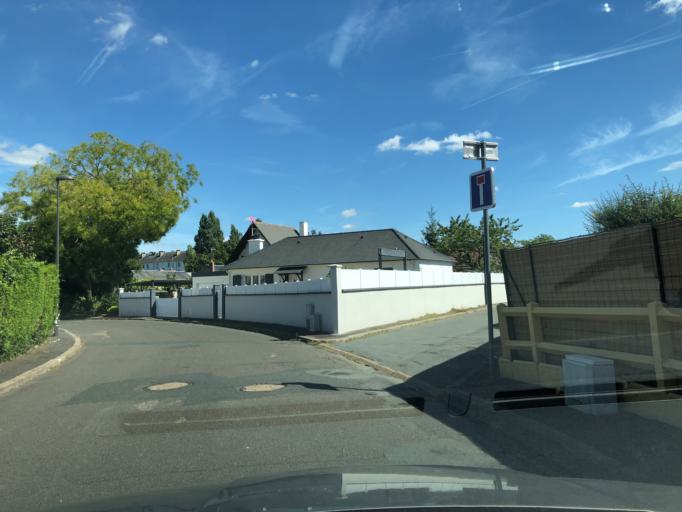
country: FR
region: Centre
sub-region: Departement d'Indre-et-Loire
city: Saint-Cyr-sur-Loire
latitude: 47.4240
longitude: 0.6878
